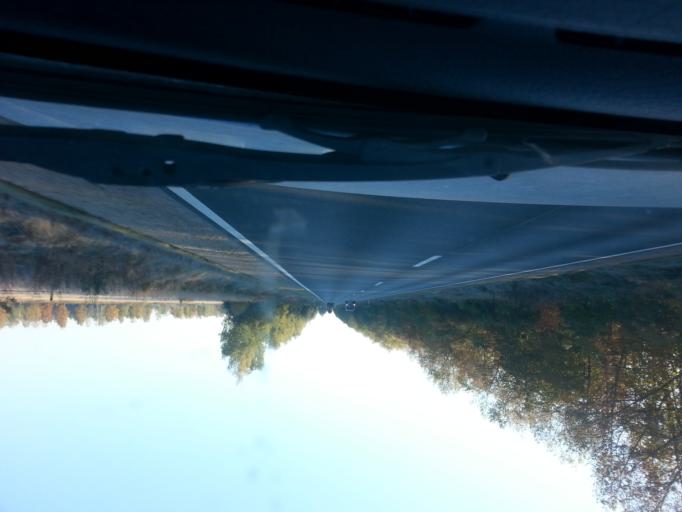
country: LV
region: Jelgava
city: Jelgava
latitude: 56.5148
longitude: 23.7027
